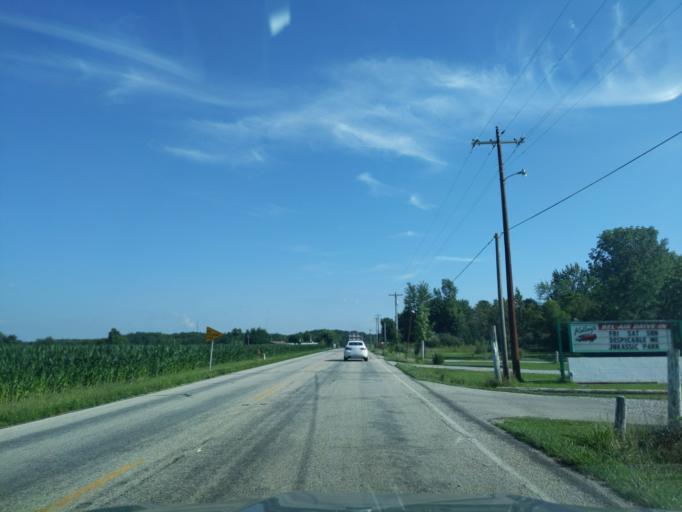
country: US
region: Indiana
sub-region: Ripley County
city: Versailles
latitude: 39.0797
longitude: -85.2724
